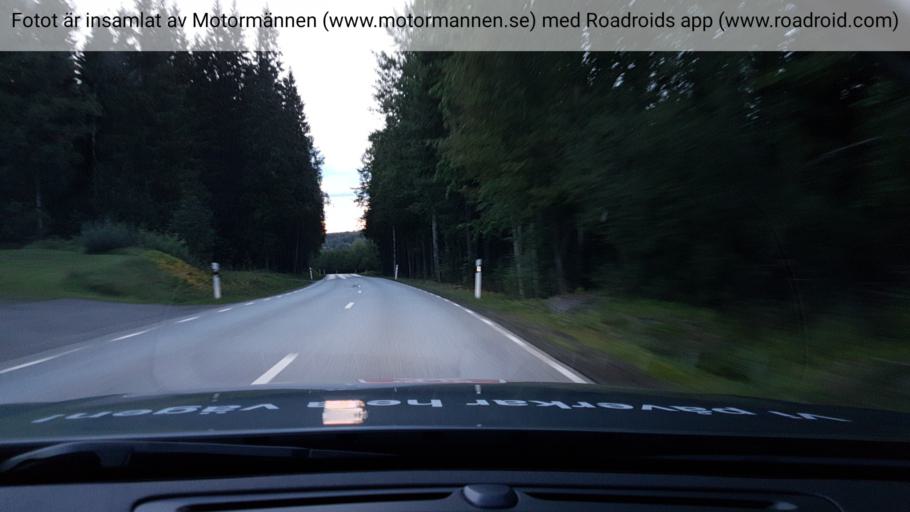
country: SE
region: OErebro
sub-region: Ljusnarsbergs Kommun
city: Kopparberg
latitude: 59.8649
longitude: 15.0033
